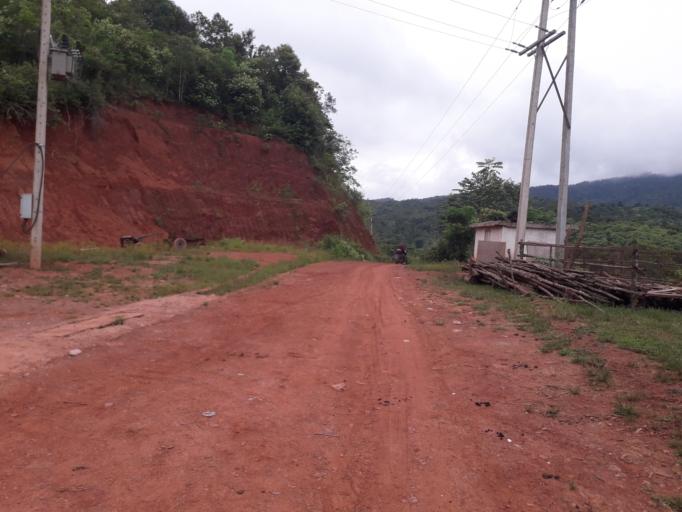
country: CN
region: Yunnan
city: Menglie
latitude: 22.2278
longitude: 101.6244
